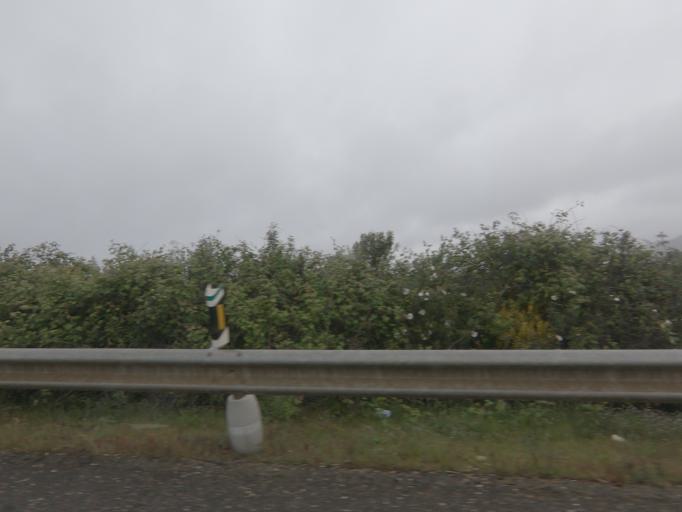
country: ES
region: Extremadura
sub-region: Provincia de Badajoz
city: Puebla de Obando
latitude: 39.1696
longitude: -6.6289
